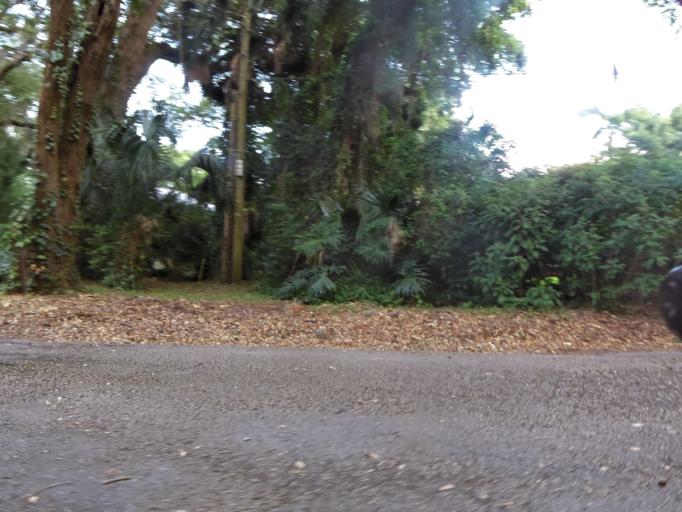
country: US
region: Florida
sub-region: Duval County
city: Jacksonville
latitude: 30.3104
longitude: -81.6267
